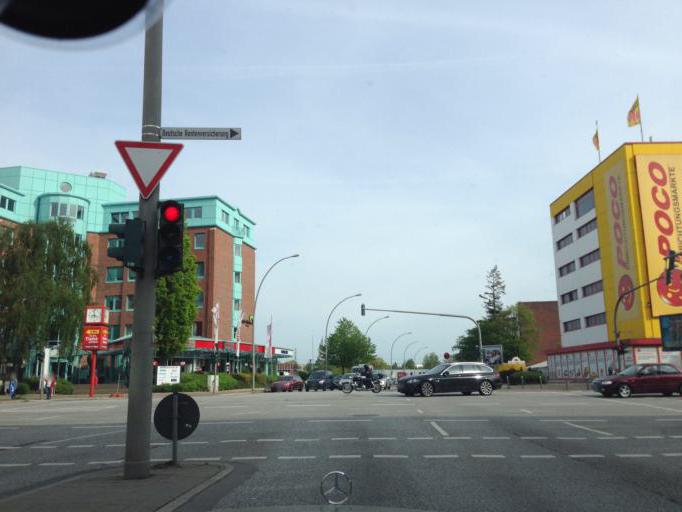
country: DE
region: Hamburg
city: Wandsbek
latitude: 53.5887
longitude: 10.0990
